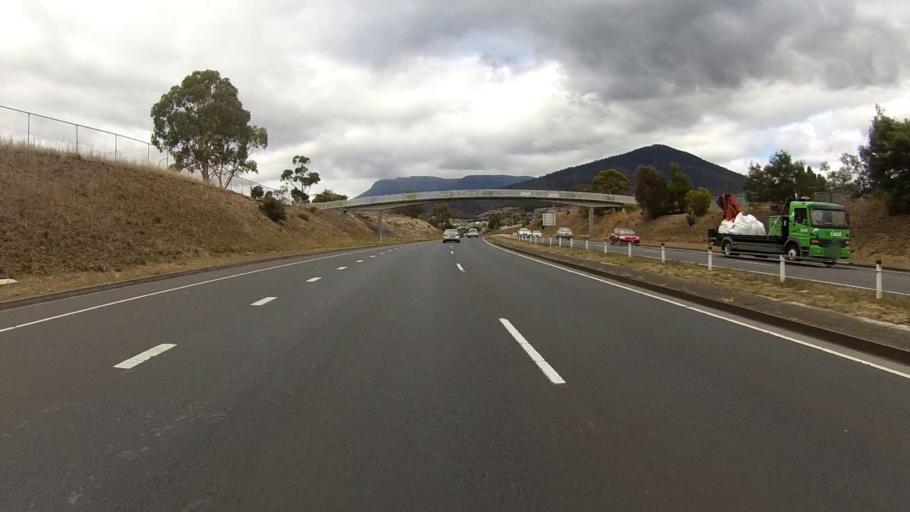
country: AU
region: Tasmania
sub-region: Glenorchy
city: Berriedale
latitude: -42.8035
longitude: 147.2499
